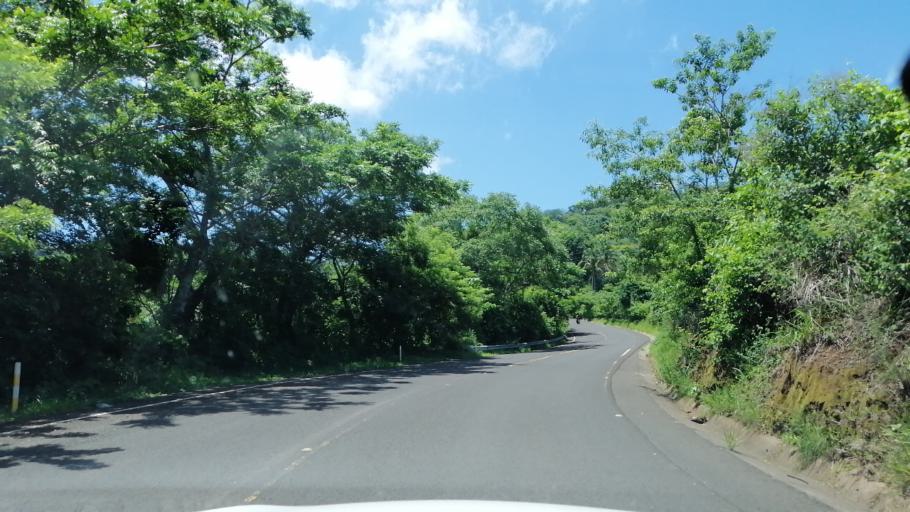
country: SV
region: San Miguel
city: Ciudad Barrios
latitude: 13.8025
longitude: -88.2992
